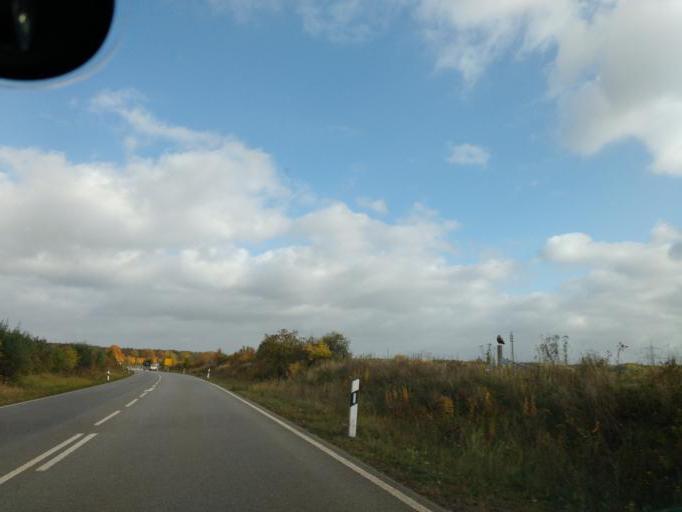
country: DE
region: Brandenburg
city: Altlandsberg
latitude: 52.5591
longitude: 13.7571
